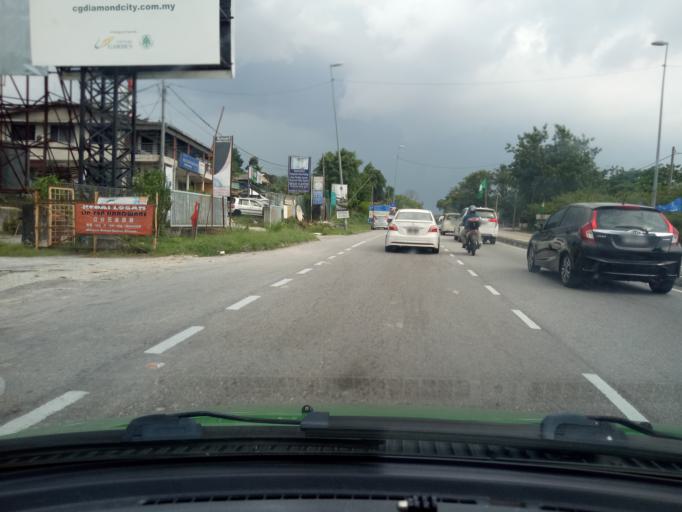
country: MY
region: Selangor
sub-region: Hulu Langat
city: Semenyih
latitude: 2.9441
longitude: 101.8488
